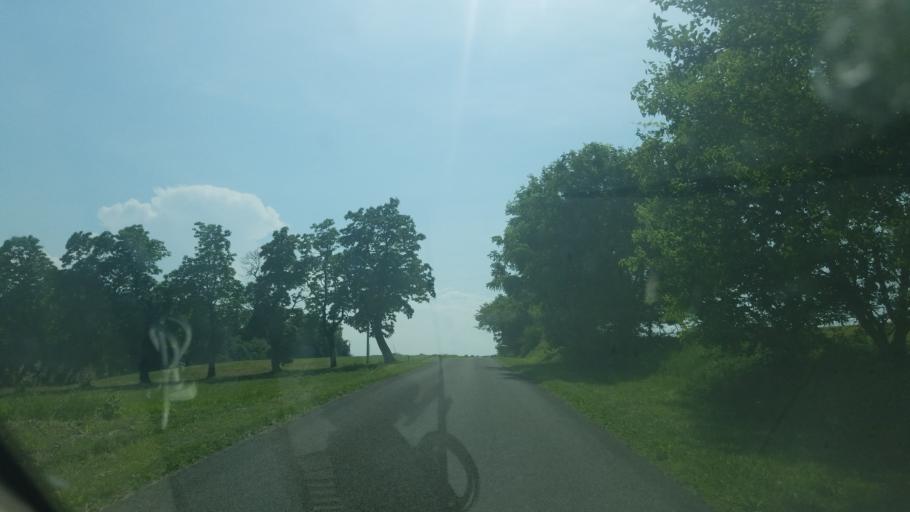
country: US
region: Ohio
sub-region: Champaign County
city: North Lewisburg
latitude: 40.2760
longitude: -83.6479
